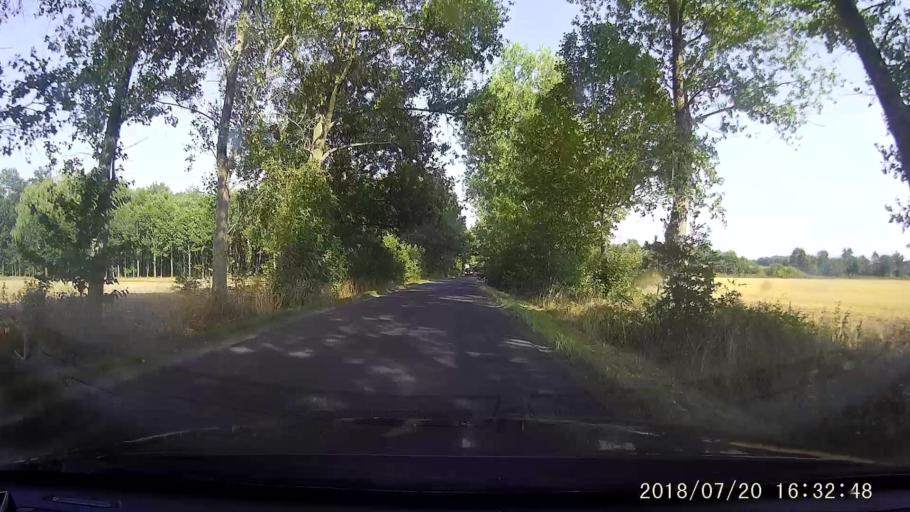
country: PL
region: Lower Silesian Voivodeship
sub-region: Powiat zgorzelecki
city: Sulikow
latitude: 51.0935
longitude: 15.0908
